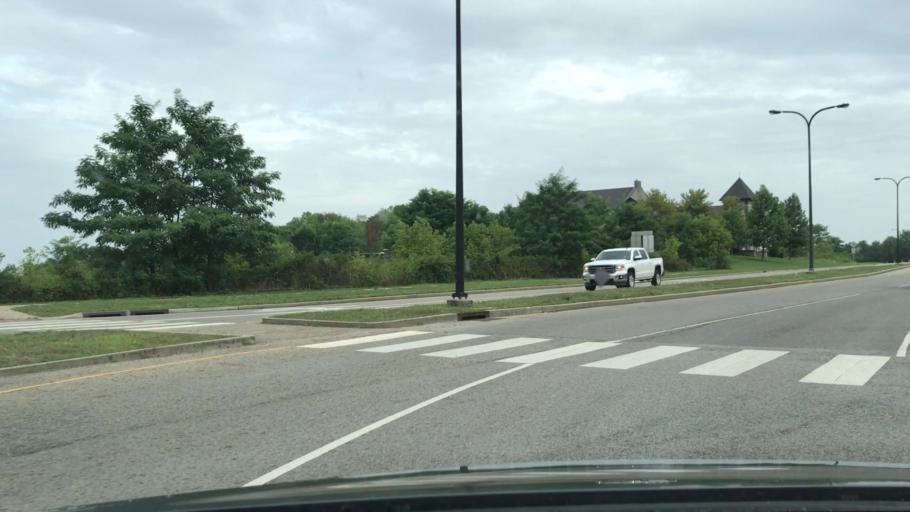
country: US
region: Tennessee
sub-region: Williamson County
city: Franklin
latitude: 35.9323
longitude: -86.7941
